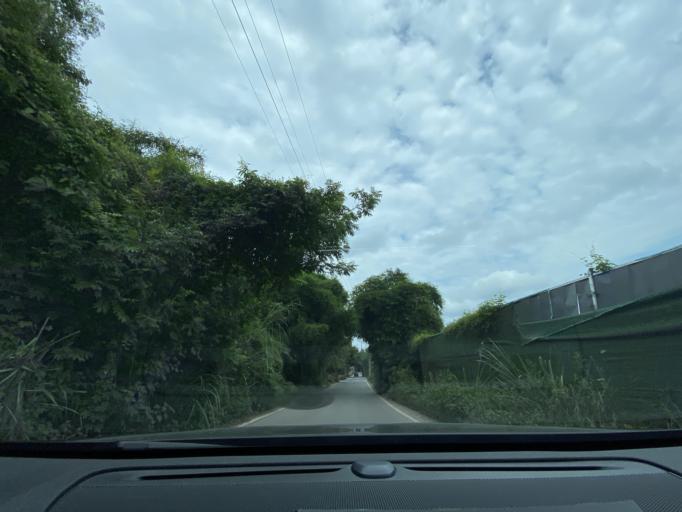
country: CN
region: Sichuan
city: Jiancheng
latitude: 30.4340
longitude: 104.5250
